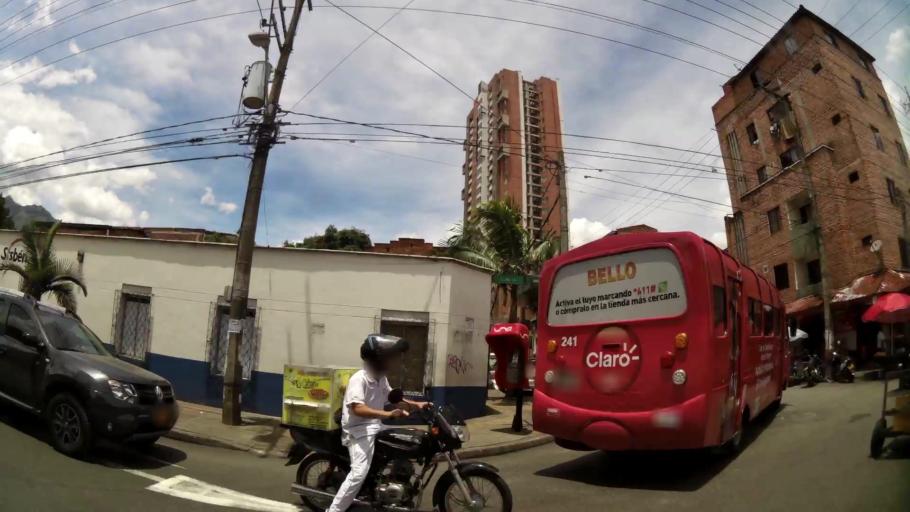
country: CO
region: Antioquia
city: Bello
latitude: 6.3305
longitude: -75.5560
